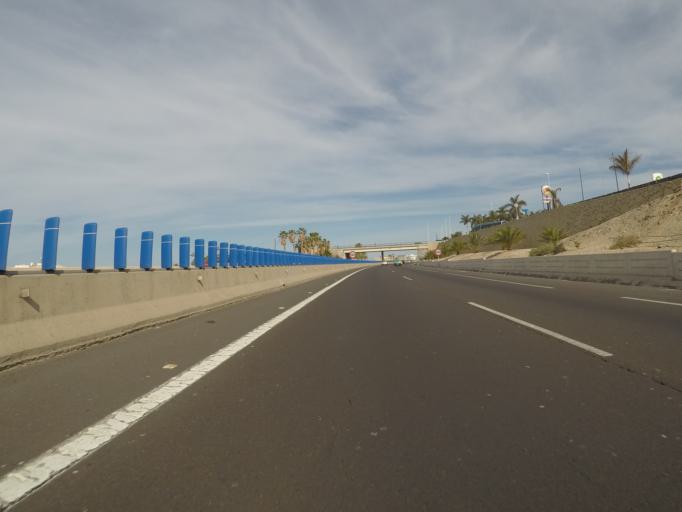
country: ES
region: Canary Islands
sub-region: Provincia de Santa Cruz de Tenerife
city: Playa de las Americas
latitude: 28.0680
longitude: -16.7235
